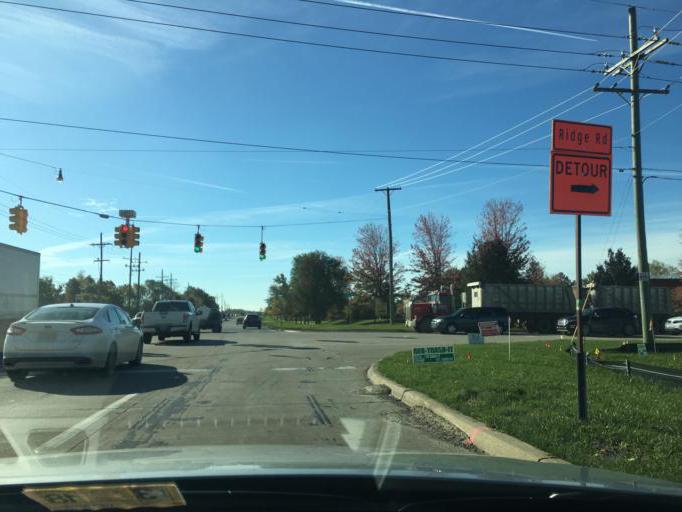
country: US
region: Michigan
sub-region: Wayne County
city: Northville
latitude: 42.3946
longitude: -83.5103
